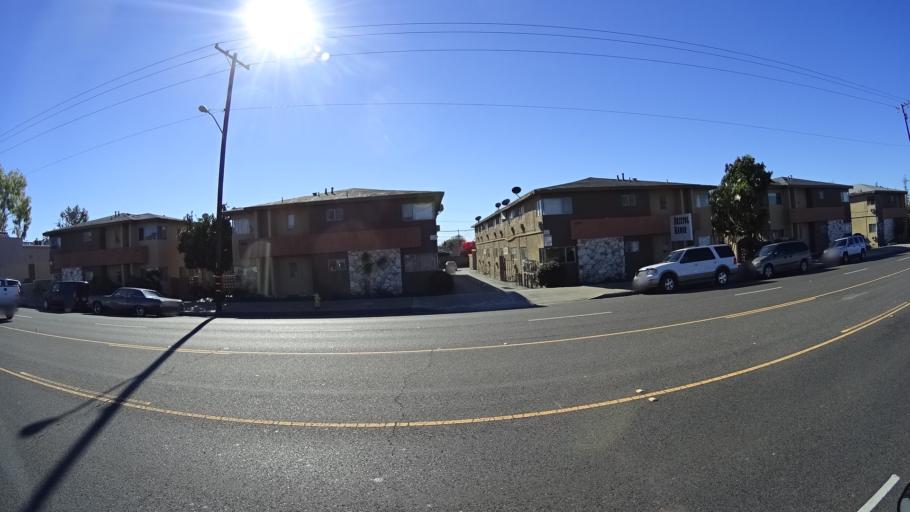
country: US
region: California
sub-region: Los Angeles County
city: East La Mirada
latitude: 33.9399
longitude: -117.9747
